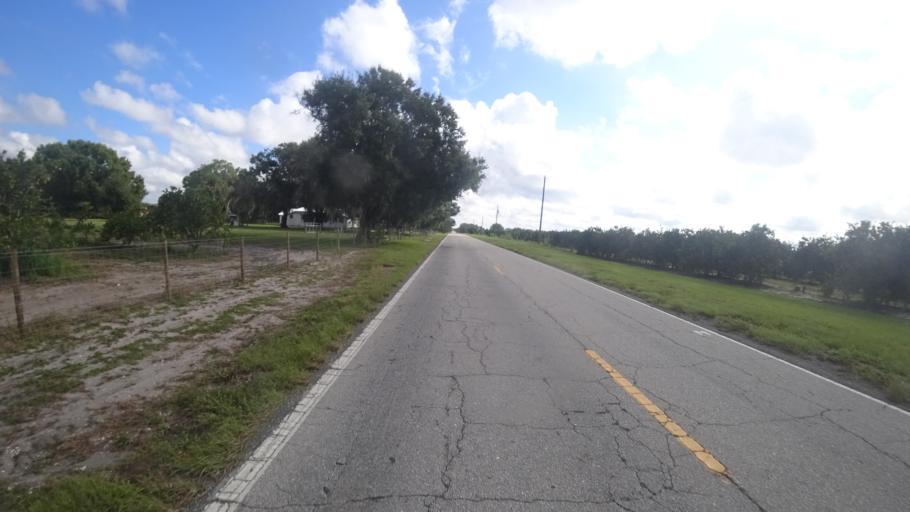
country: US
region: Florida
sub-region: Hillsborough County
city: Wimauma
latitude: 27.5373
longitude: -82.0899
